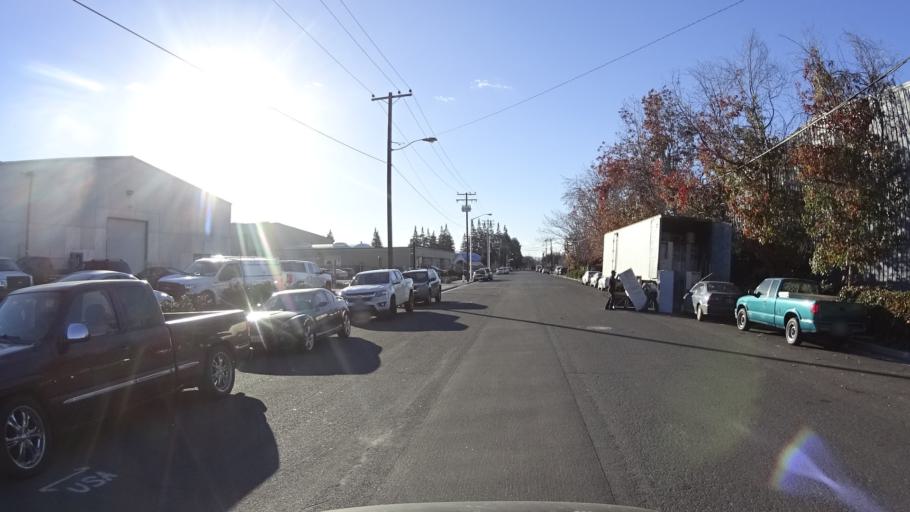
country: US
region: California
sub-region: Santa Clara County
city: Santa Clara
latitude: 37.3701
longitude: -121.9469
